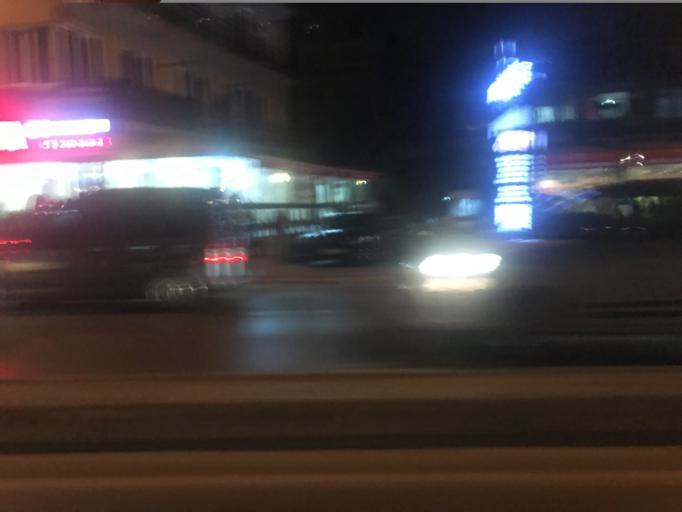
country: TR
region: Istanbul
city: Bahcelievler
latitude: 40.9893
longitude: 28.8714
